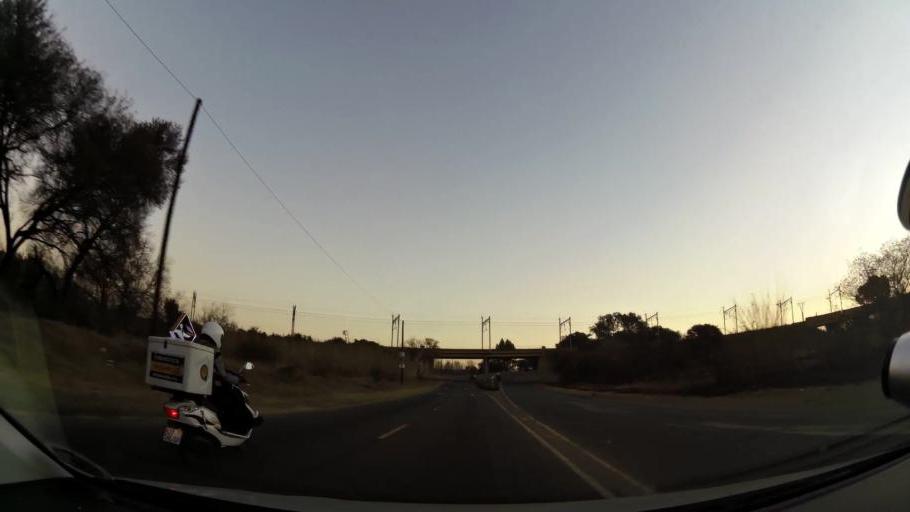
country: ZA
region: Gauteng
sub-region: City of Tshwane Metropolitan Municipality
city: Pretoria
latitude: -25.7372
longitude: 28.1649
